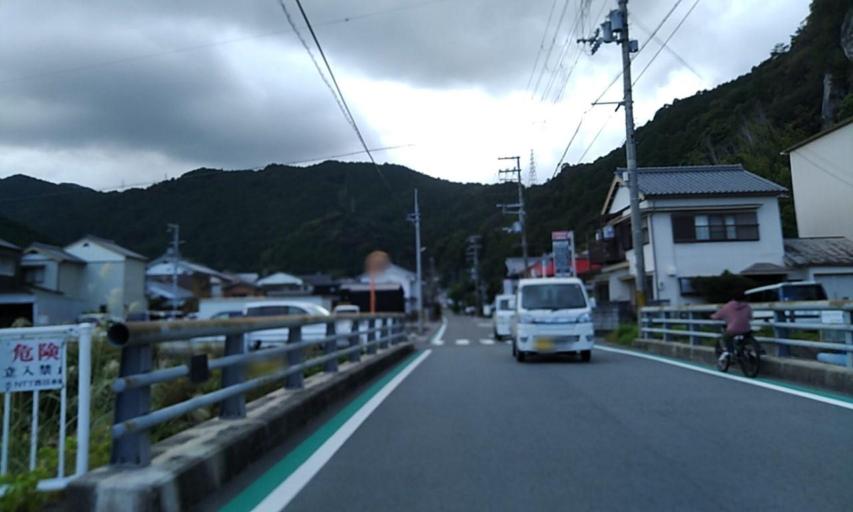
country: JP
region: Wakayama
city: Shingu
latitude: 33.7214
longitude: 135.9839
